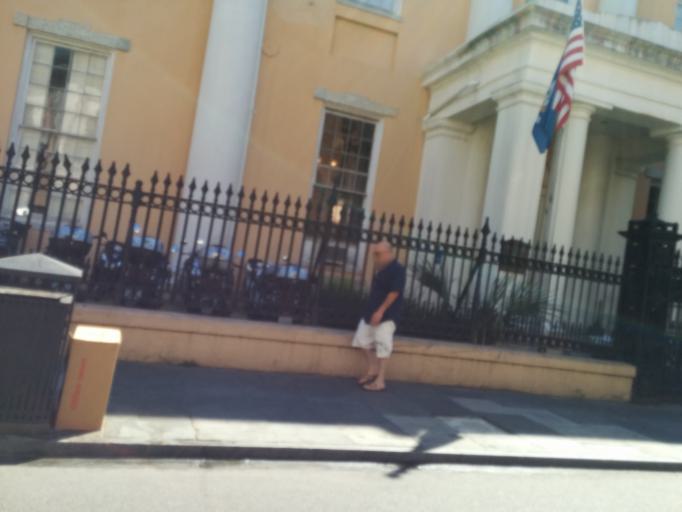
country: US
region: Louisiana
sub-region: Orleans Parish
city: New Orleans
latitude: 29.9556
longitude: -90.0670
